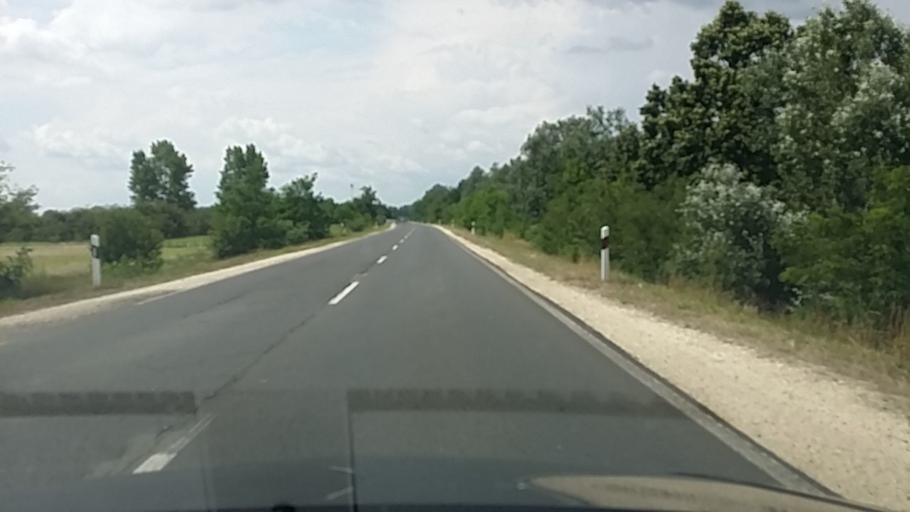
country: HU
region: Pest
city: Taborfalva
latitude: 47.0854
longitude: 19.4846
